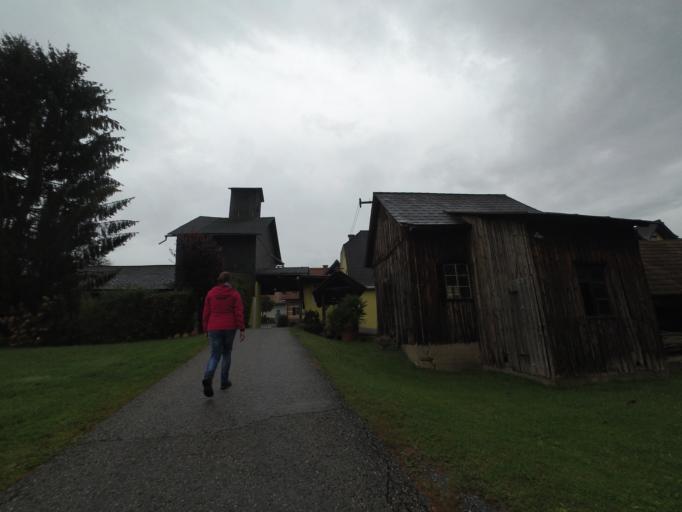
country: AT
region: Styria
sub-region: Politischer Bezirk Deutschlandsberg
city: Sankt Martin im Sulmtal
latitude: 46.7544
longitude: 15.2907
